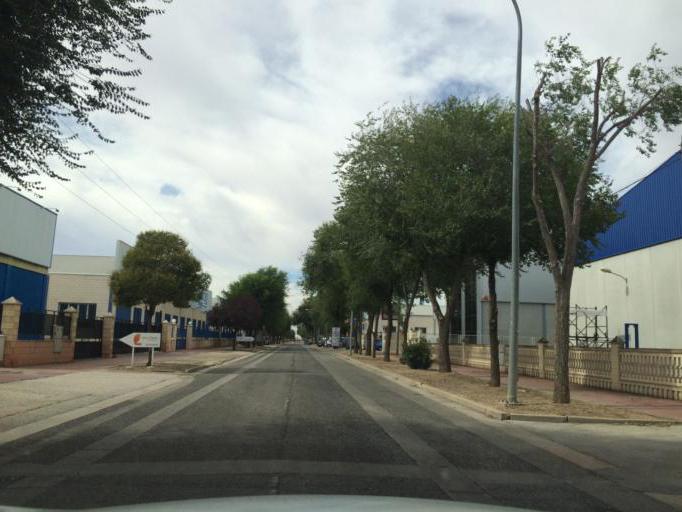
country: ES
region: Castille-La Mancha
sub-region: Provincia de Albacete
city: Albacete
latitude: 39.0181
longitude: -1.8859
